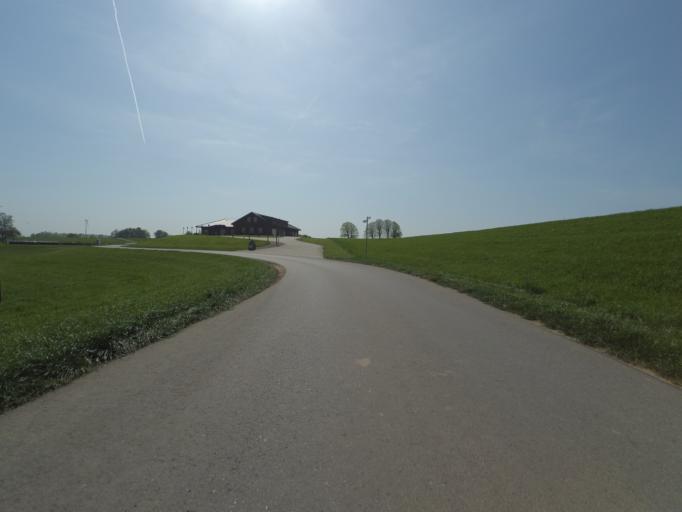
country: DE
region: North Rhine-Westphalia
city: Rees
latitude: 51.7188
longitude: 6.4378
